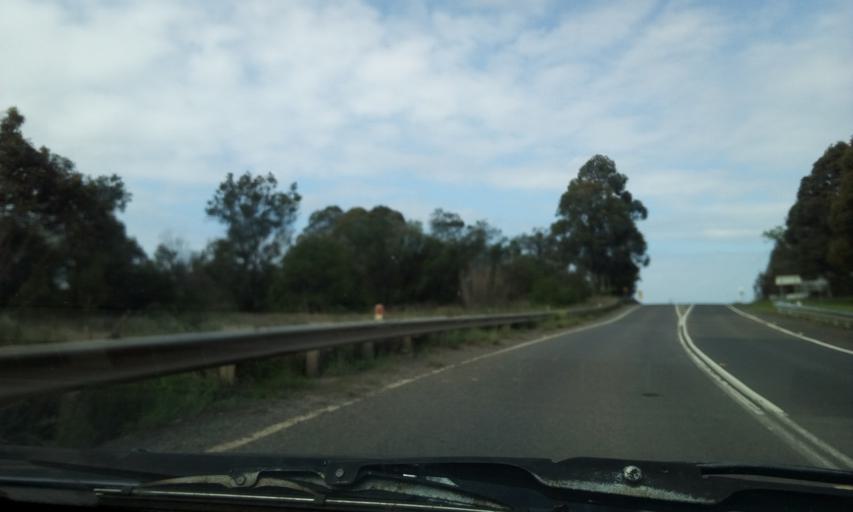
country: AU
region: New South Wales
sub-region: Campbelltown Municipality
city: Glen Alpine
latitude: -34.1171
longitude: 150.7398
